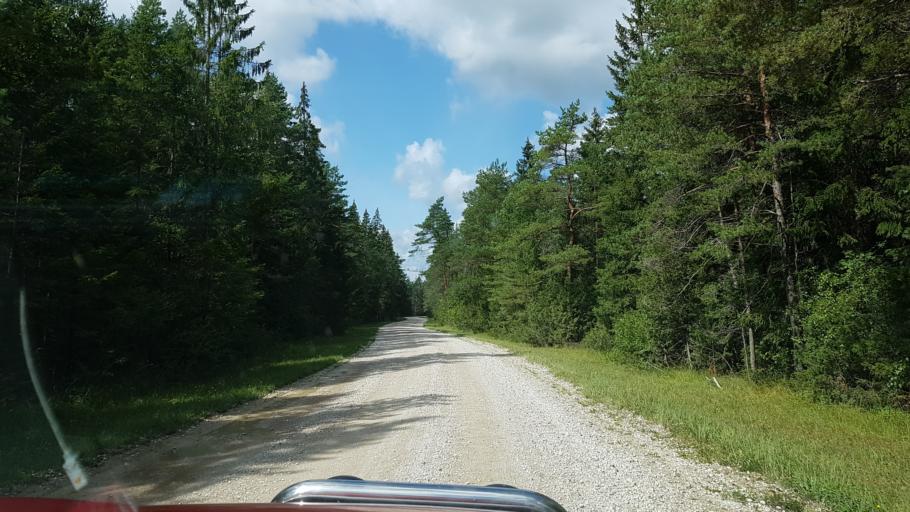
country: EE
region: Raplamaa
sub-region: Rapla vald
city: Rapla
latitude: 58.9580
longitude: 24.6538
